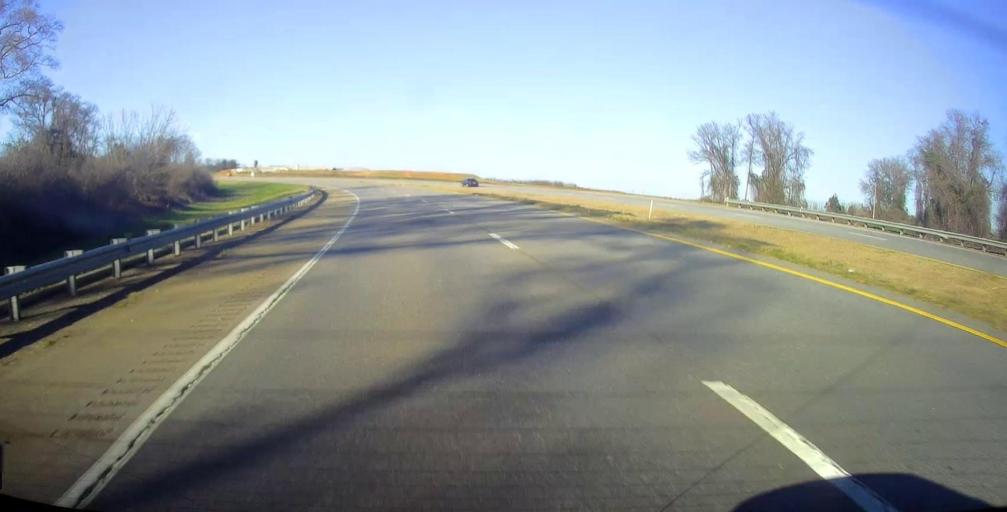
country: US
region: Georgia
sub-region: Sumter County
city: Americus
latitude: 31.9751
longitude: -84.2472
